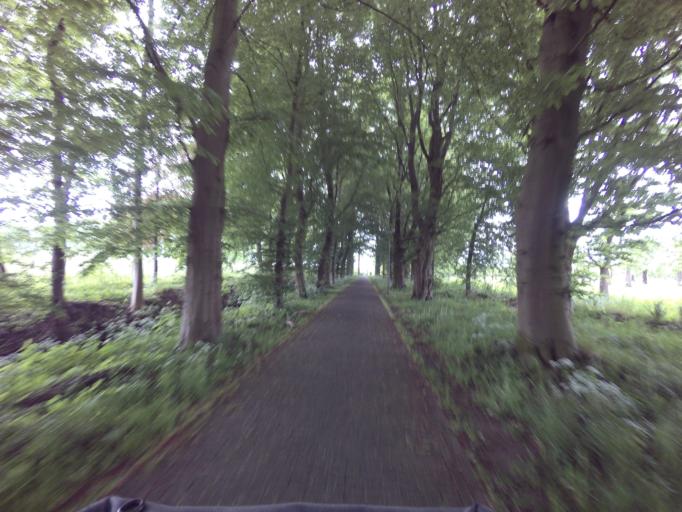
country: NL
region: Utrecht
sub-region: Gemeente Lopik
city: Lopik
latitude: 51.9602
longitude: 4.9498
